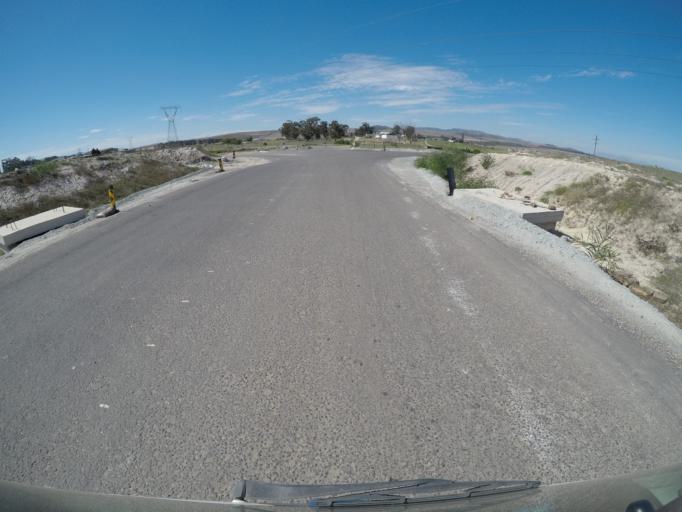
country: ZA
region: Western Cape
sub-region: West Coast District Municipality
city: Malmesbury
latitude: -33.5124
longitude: 18.6579
